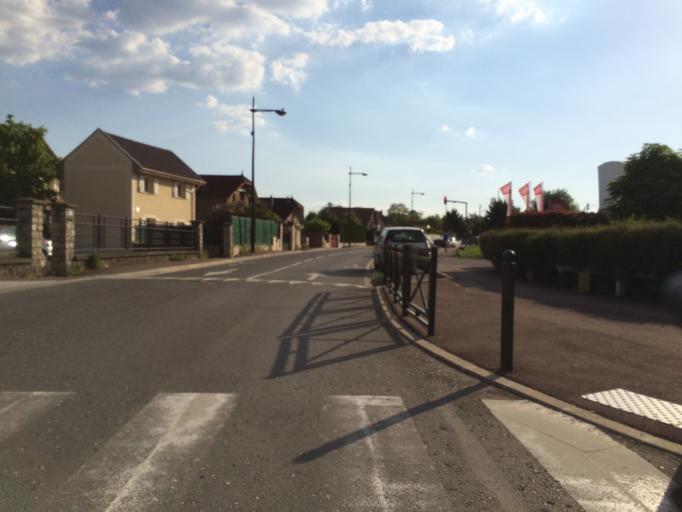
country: FR
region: Ile-de-France
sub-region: Departement de l'Essonne
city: Villabe
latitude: 48.6081
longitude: 2.4568
